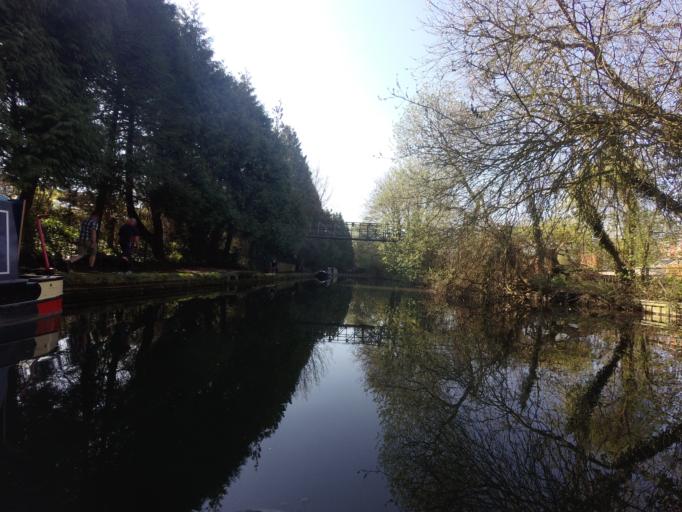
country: GB
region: England
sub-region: Hertfordshire
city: Kings Langley
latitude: 51.7313
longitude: -0.4576
